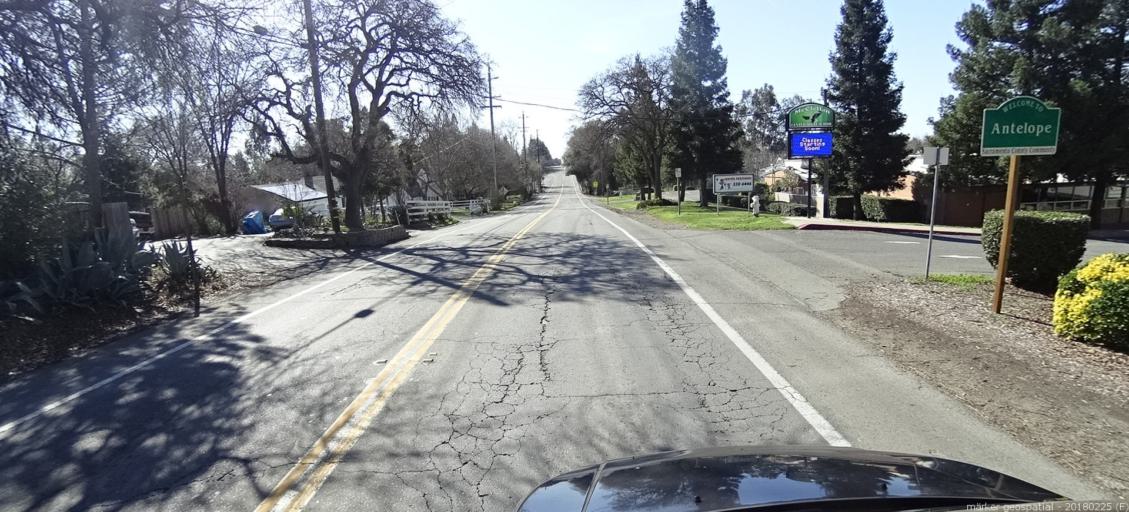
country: US
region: California
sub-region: Sacramento County
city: North Highlands
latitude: 38.7284
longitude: -121.3925
